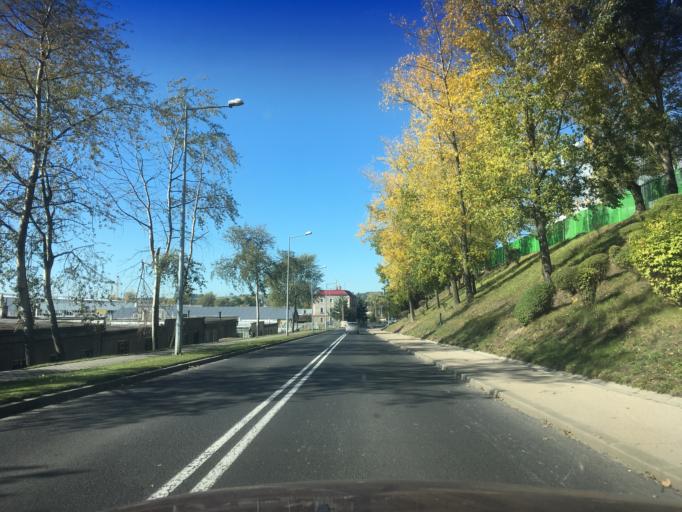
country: DE
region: Saxony
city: Hirschfelde
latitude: 50.9458
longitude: 14.9108
